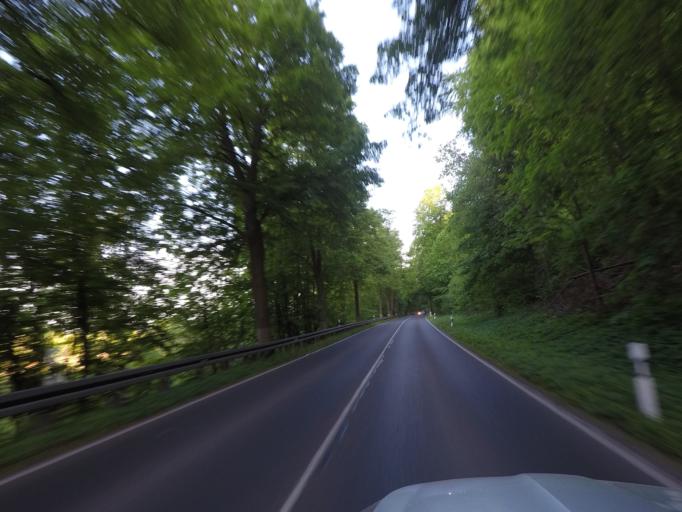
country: DE
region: Brandenburg
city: Falkenberg
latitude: 52.7995
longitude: 13.9744
